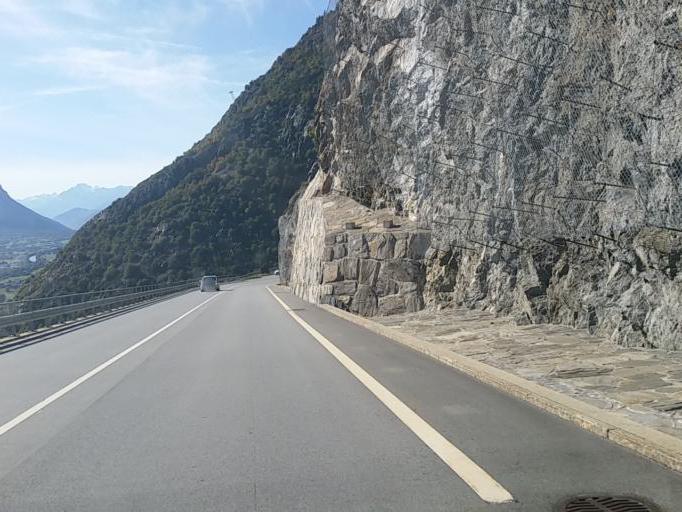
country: CH
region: Valais
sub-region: Leuk District
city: Gampel
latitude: 46.3197
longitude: 7.7502
